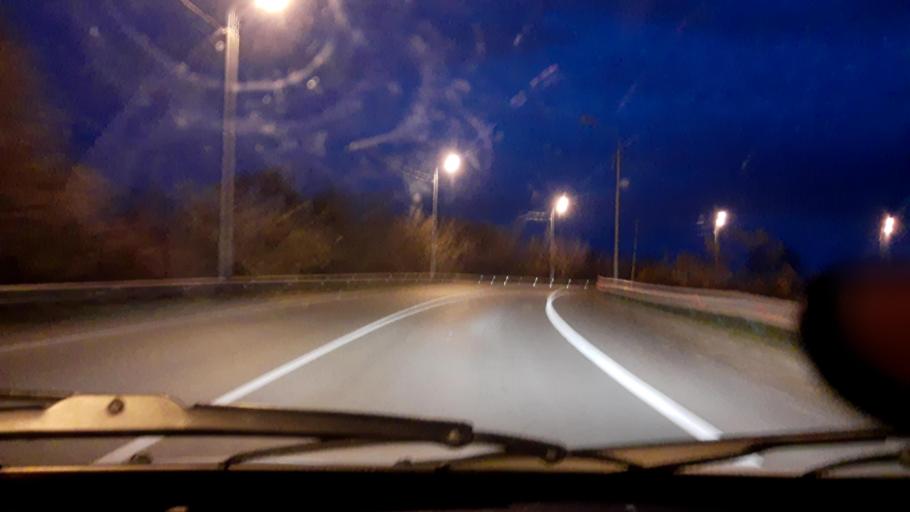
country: RU
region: Bashkortostan
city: Blagoveshchensk
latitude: 54.9095
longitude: 56.0663
